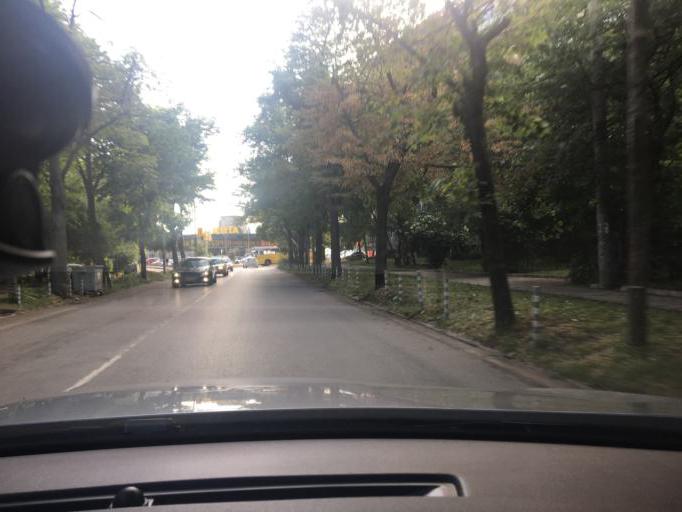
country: BG
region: Sofia-Capital
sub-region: Stolichna Obshtina
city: Sofia
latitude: 42.6842
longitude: 23.2995
